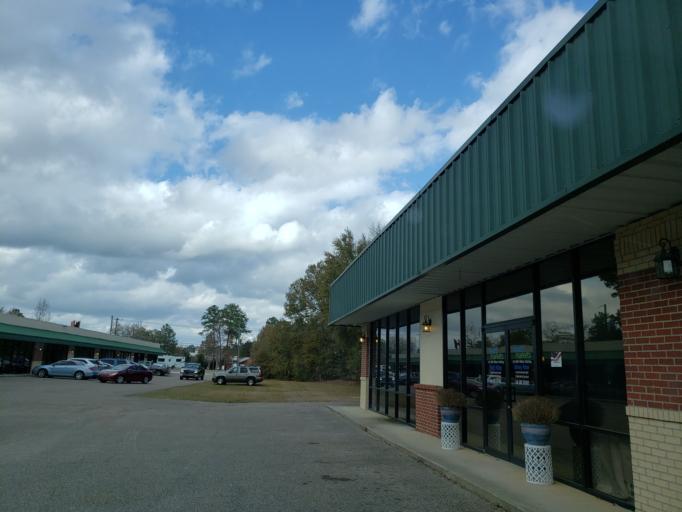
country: US
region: Mississippi
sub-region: Lamar County
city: West Hattiesburg
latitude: 31.3173
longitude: -89.3615
